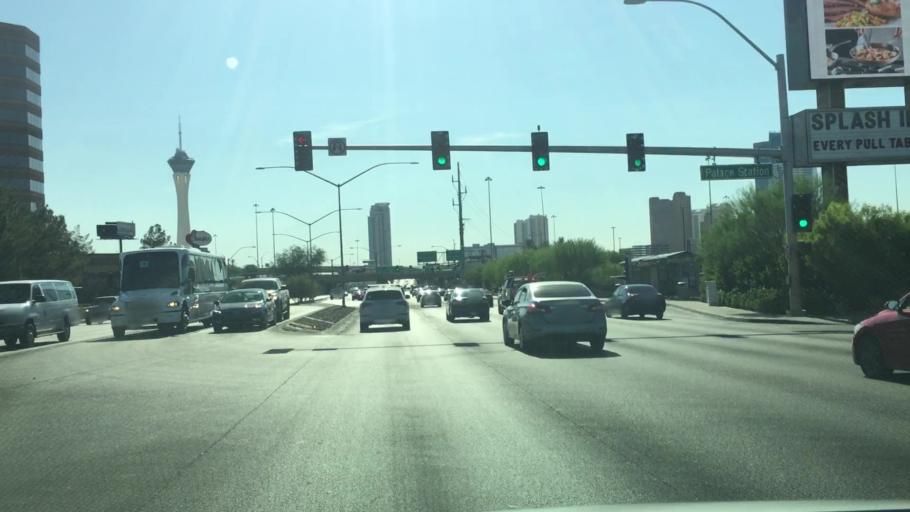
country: US
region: Nevada
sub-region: Clark County
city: Las Vegas
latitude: 36.1442
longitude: -115.1754
